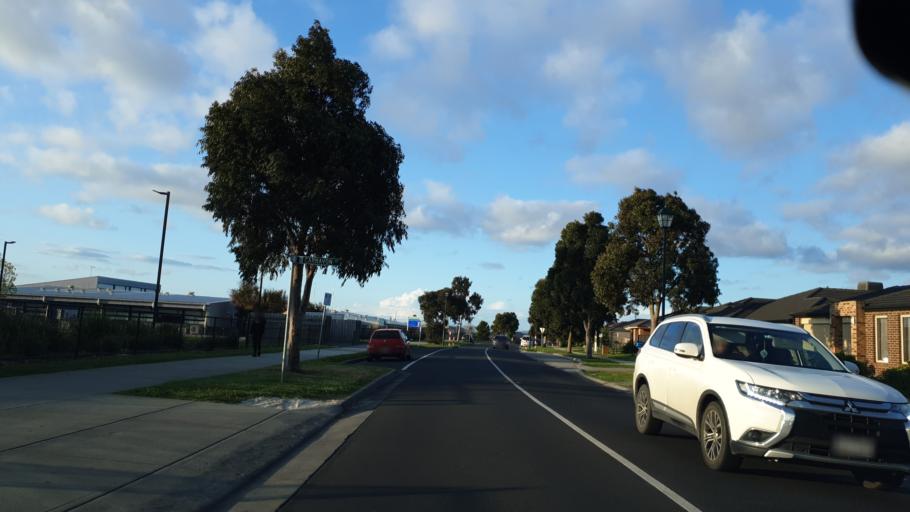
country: AU
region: Victoria
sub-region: Casey
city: Cranbourne East
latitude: -38.1057
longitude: 145.3061
